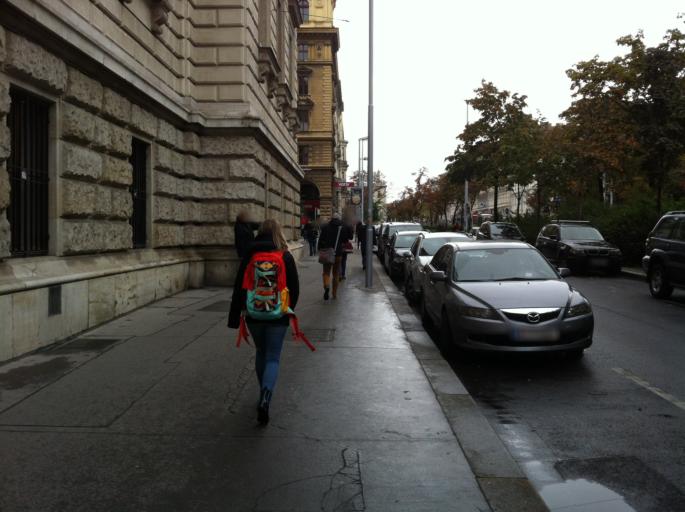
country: AT
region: Vienna
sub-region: Wien Stadt
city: Vienna
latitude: 48.2139
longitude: 16.3602
